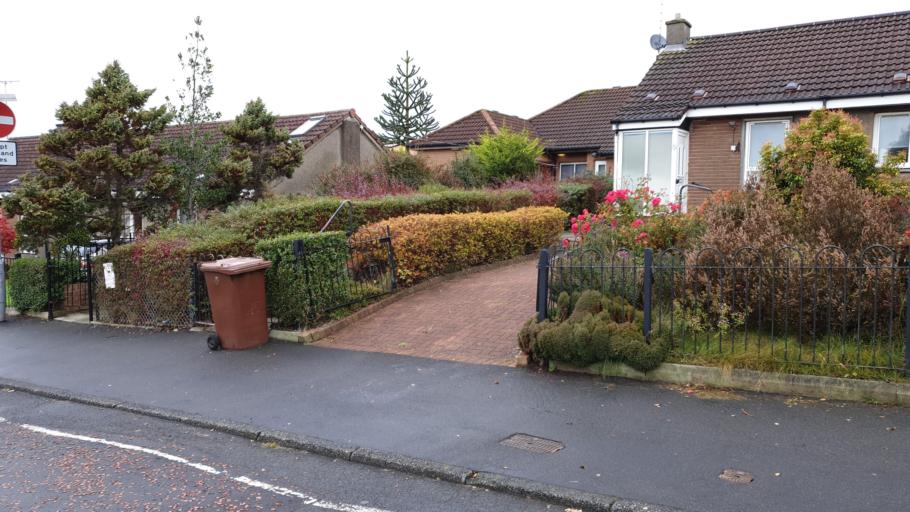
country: GB
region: Scotland
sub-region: West Dunbartonshire
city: Clydebank
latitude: 55.9085
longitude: -4.3967
